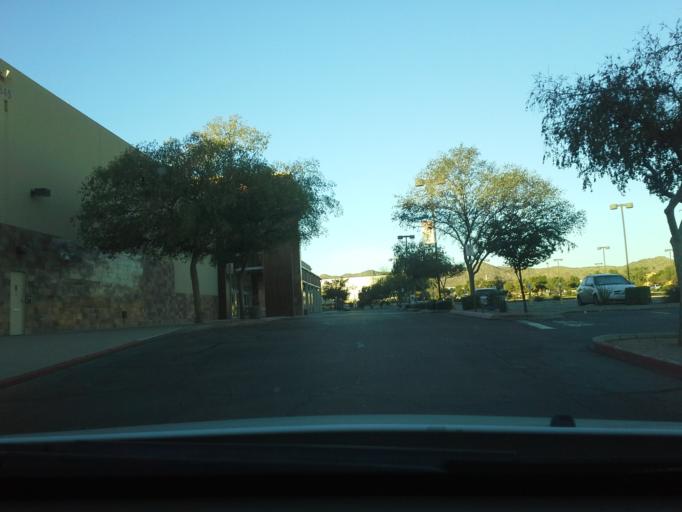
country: US
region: Arizona
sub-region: Maricopa County
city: Guadalupe
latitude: 33.3474
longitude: -111.9590
